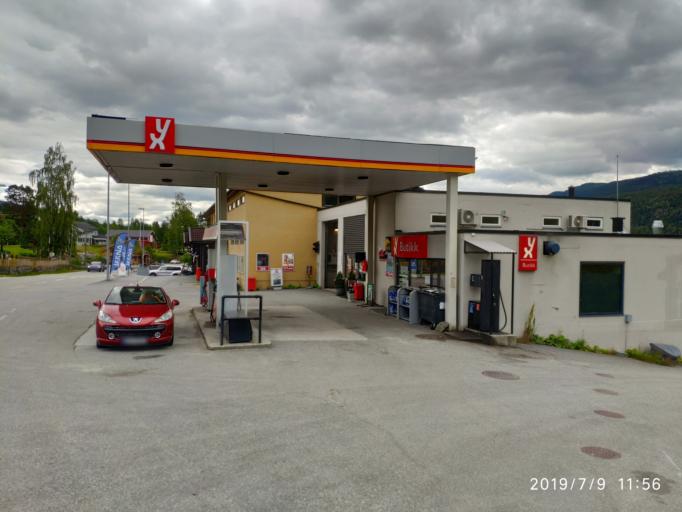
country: NO
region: Buskerud
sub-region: Fla
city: Fla
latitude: 60.2467
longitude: 9.3557
